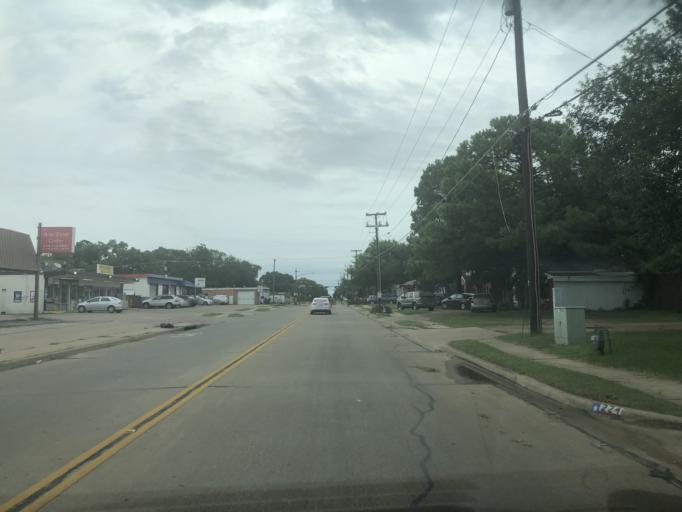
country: US
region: Texas
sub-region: Dallas County
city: Irving
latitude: 32.8086
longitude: -96.9489
